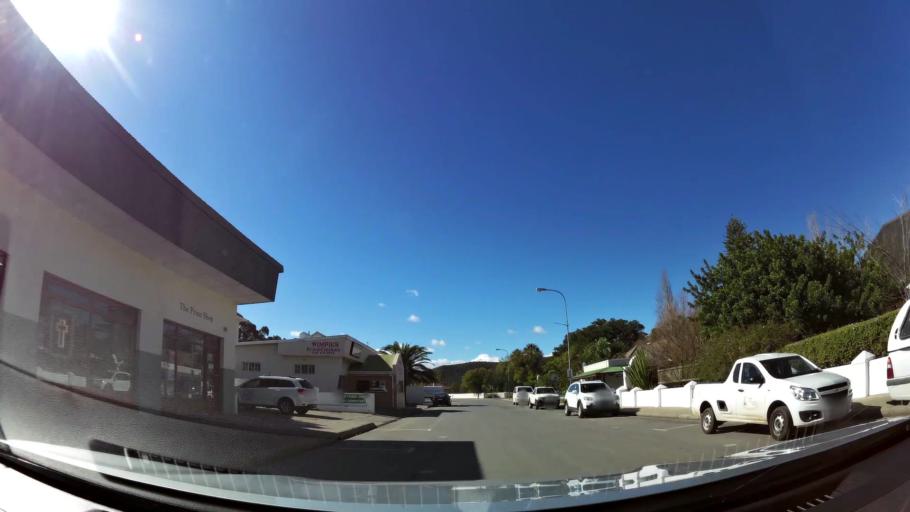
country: ZA
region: Western Cape
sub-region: Cape Winelands District Municipality
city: Ashton
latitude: -33.7858
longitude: 20.1266
